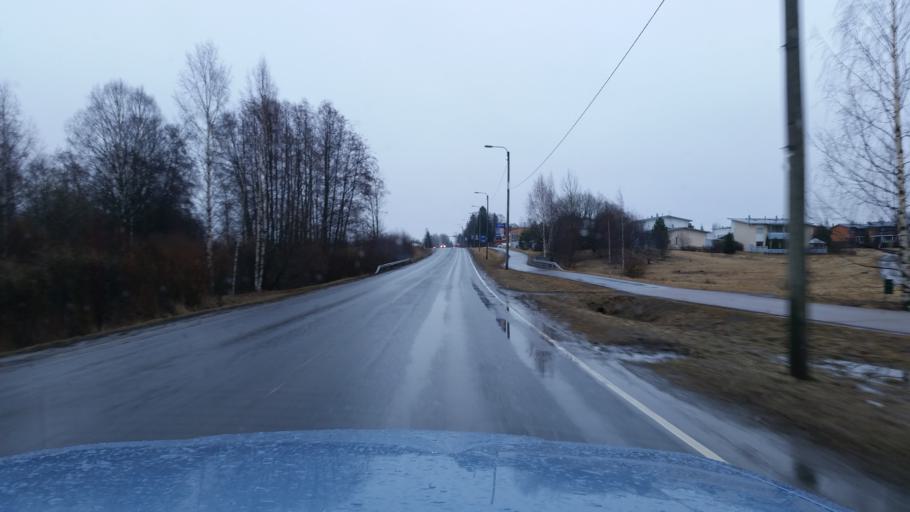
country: FI
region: Pirkanmaa
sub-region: Tampere
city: Tampere
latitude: 61.4799
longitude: 23.8184
